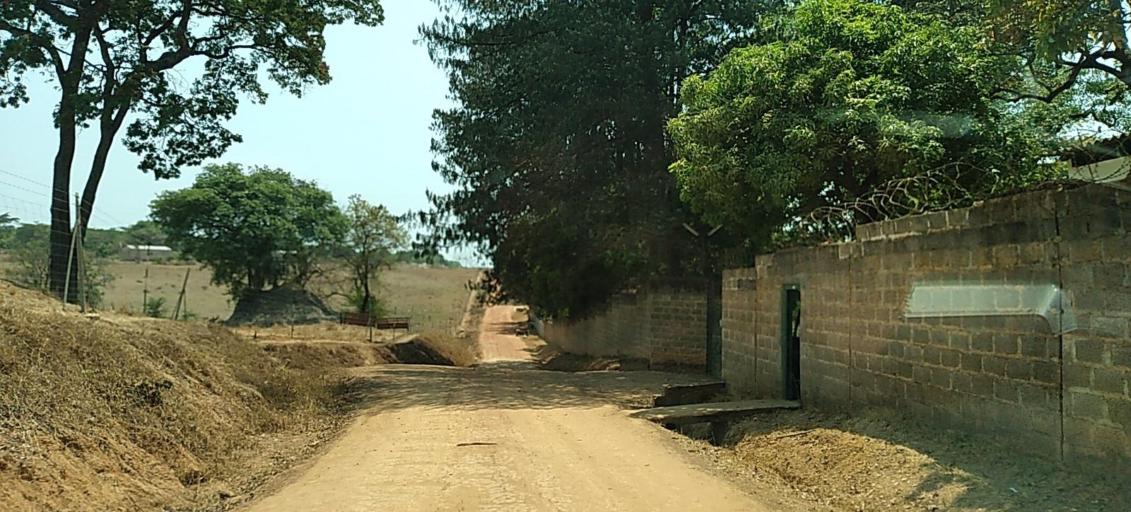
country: ZM
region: Copperbelt
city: Chambishi
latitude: -12.6230
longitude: 27.9435
